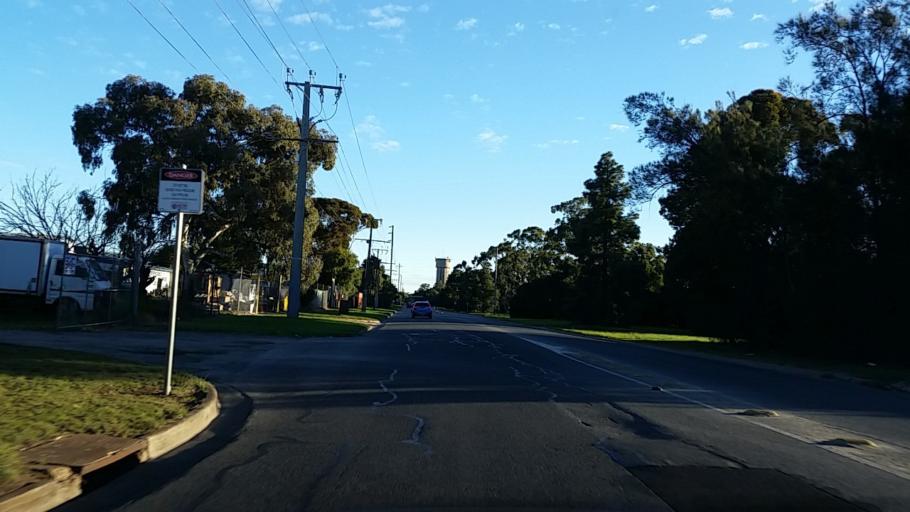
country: AU
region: South Australia
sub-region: Salisbury
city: Elizabeth
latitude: -34.7369
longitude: 138.6530
